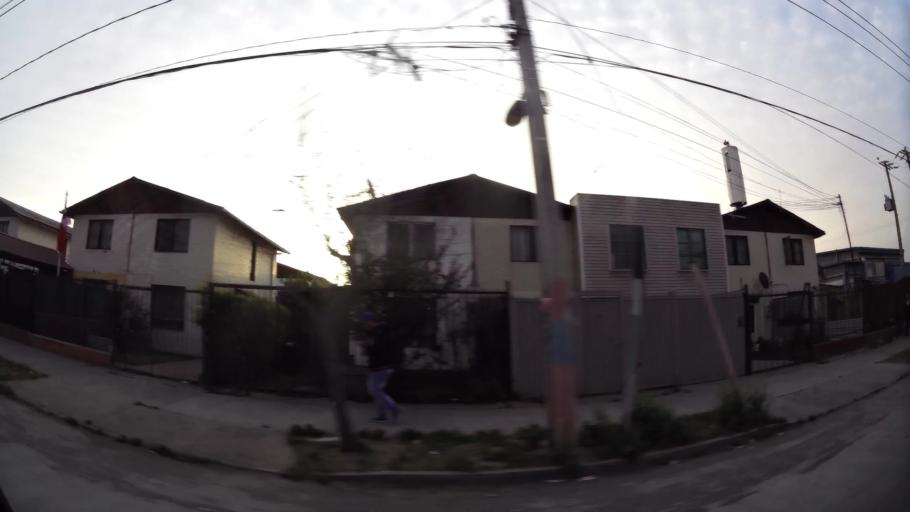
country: CL
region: Santiago Metropolitan
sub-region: Provincia de Santiago
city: Lo Prado
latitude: -33.5103
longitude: -70.7906
